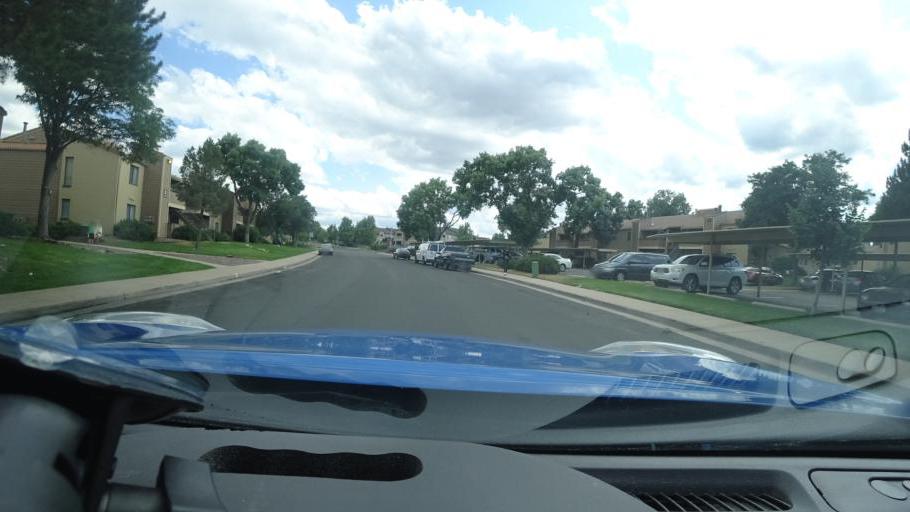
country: US
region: Colorado
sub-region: Adams County
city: Aurora
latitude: 39.6927
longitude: -104.8697
